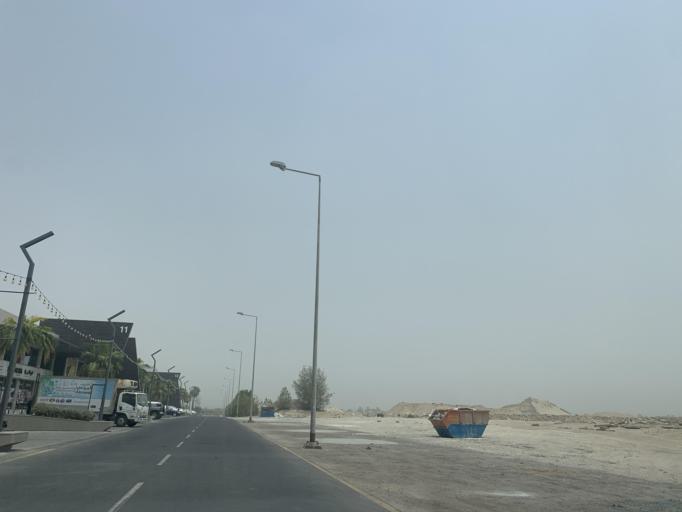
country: BH
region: Central Governorate
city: Madinat Hamad
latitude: 26.1714
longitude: 50.4811
